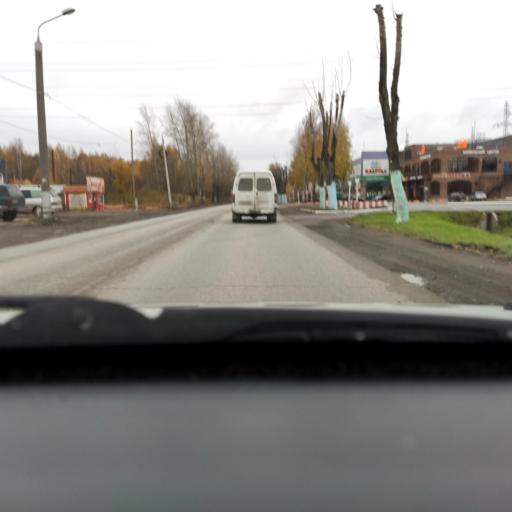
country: RU
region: Perm
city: Perm
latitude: 58.1077
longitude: 56.3624
